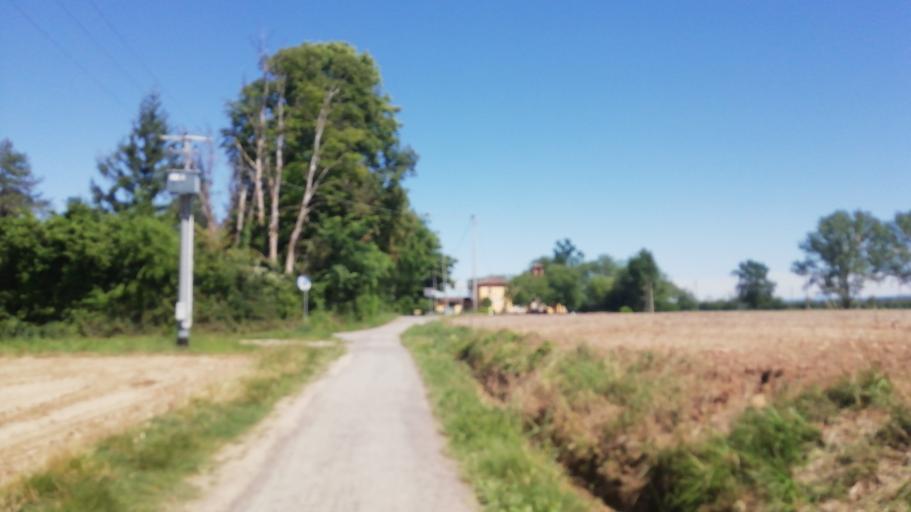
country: IT
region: Emilia-Romagna
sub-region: Provincia di Piacenza
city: Borgonovo Valtidone
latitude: 45.0012
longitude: 9.4562
